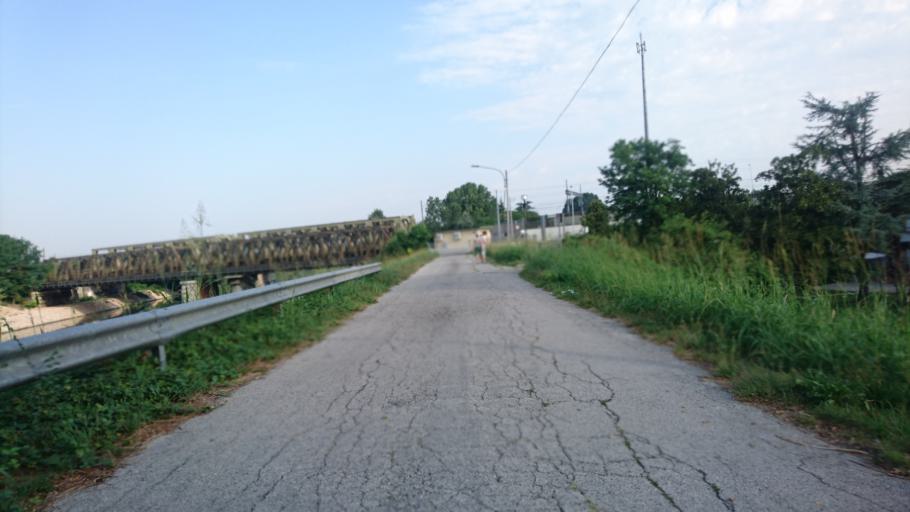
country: IT
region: Veneto
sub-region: Provincia di Padova
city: Noventa
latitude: 45.4289
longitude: 11.9509
